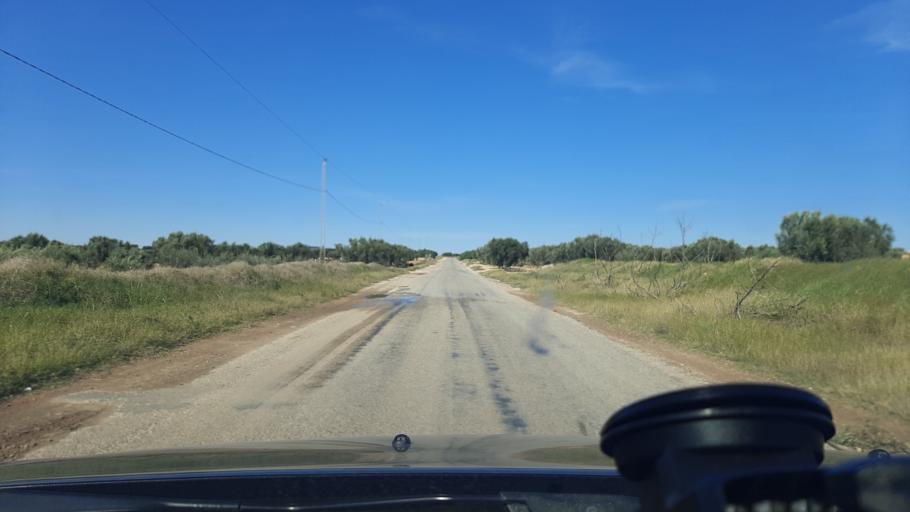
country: TN
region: Safaqis
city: Sfax
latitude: 34.9475
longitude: 10.5507
